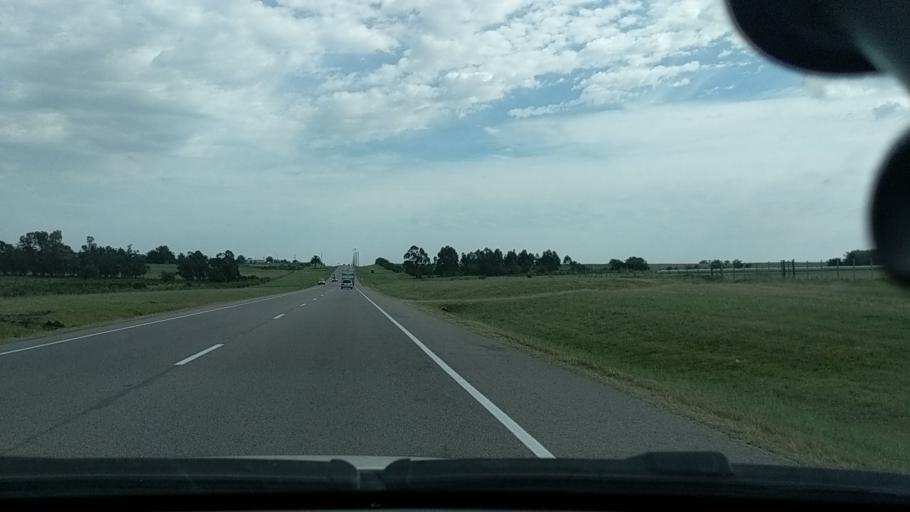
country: UY
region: Florida
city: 25 de Mayo
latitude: -34.2505
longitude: -56.2133
